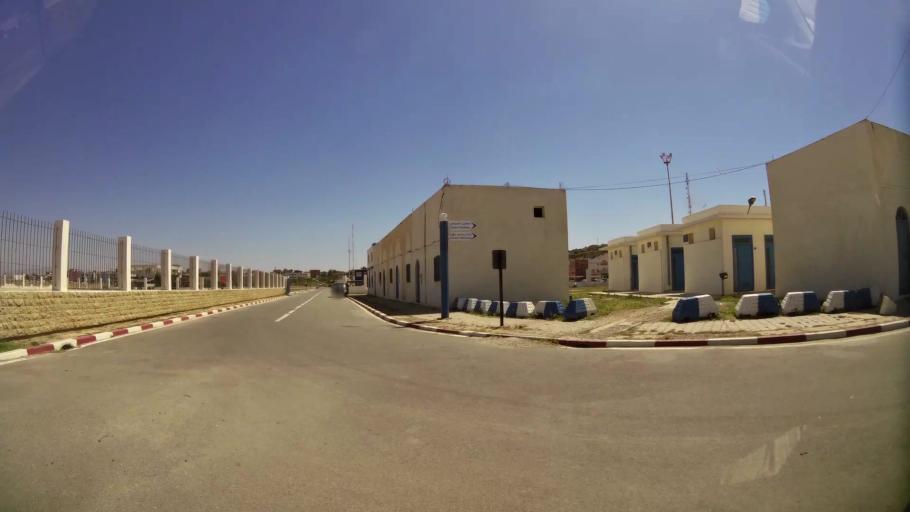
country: MA
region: Oriental
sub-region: Berkane-Taourirt
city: Madagh
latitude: 35.1436
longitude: -2.4227
